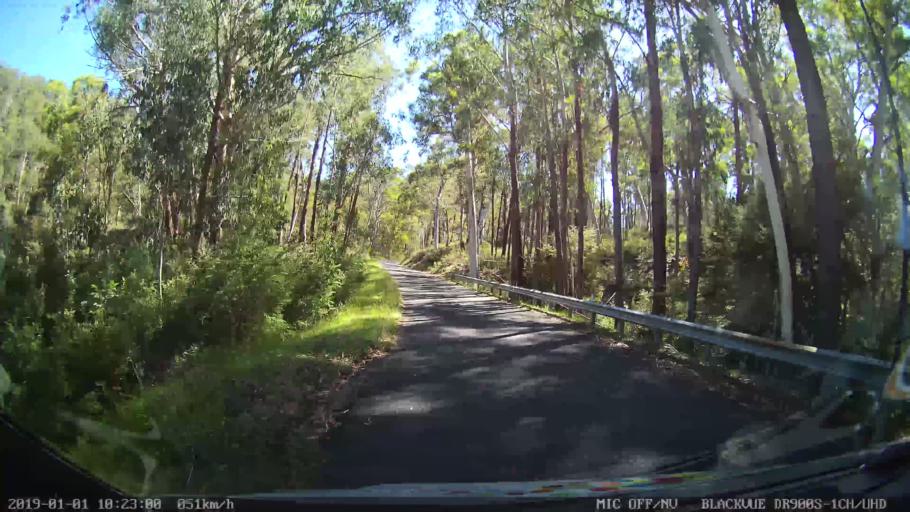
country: AU
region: New South Wales
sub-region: Snowy River
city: Jindabyne
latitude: -36.0765
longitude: 148.2087
